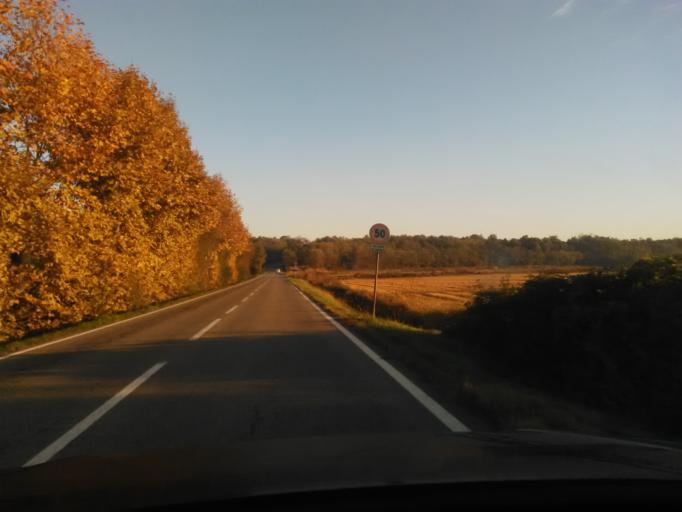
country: IT
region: Piedmont
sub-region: Provincia di Vercelli
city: Carisio
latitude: 45.3967
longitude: 8.1865
